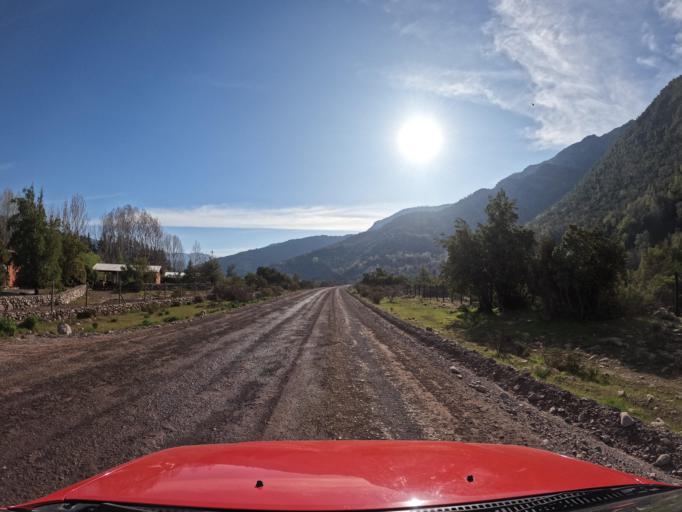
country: CL
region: O'Higgins
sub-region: Provincia de Colchagua
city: Chimbarongo
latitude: -34.9965
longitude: -70.8125
